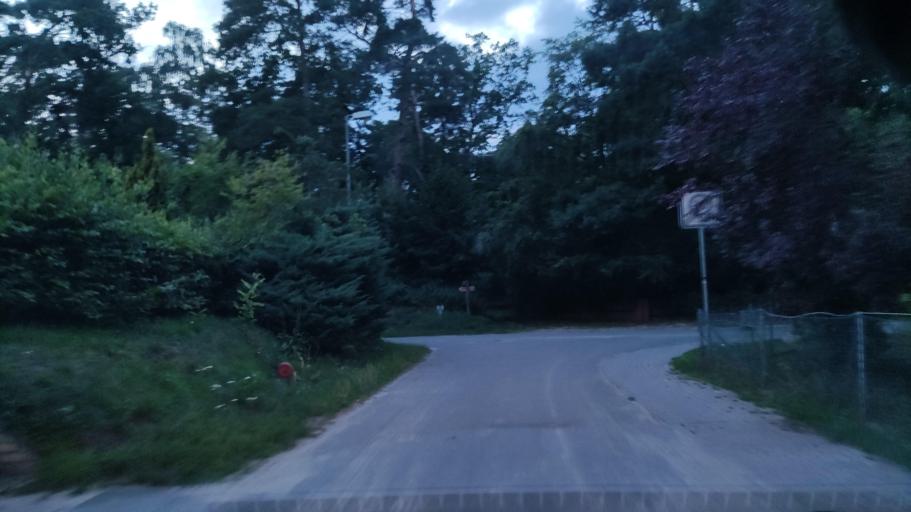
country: DE
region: Schleswig-Holstein
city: Schnakenbek
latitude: 53.3835
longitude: 10.4997
